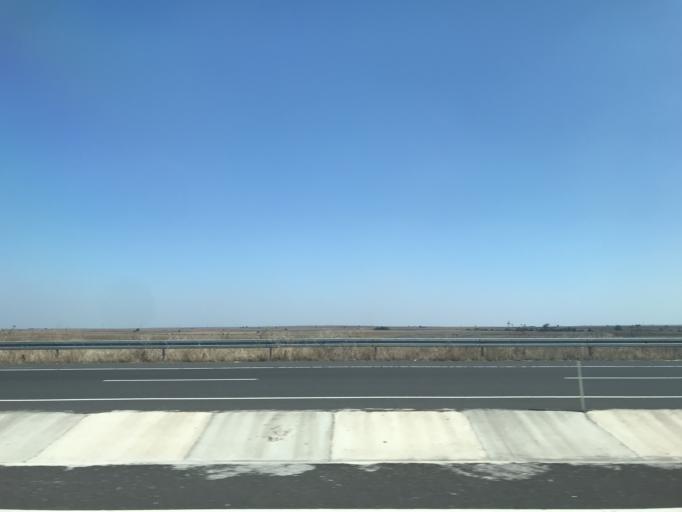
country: TR
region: Tekirdag
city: Muratli
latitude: 41.1887
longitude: 27.5396
